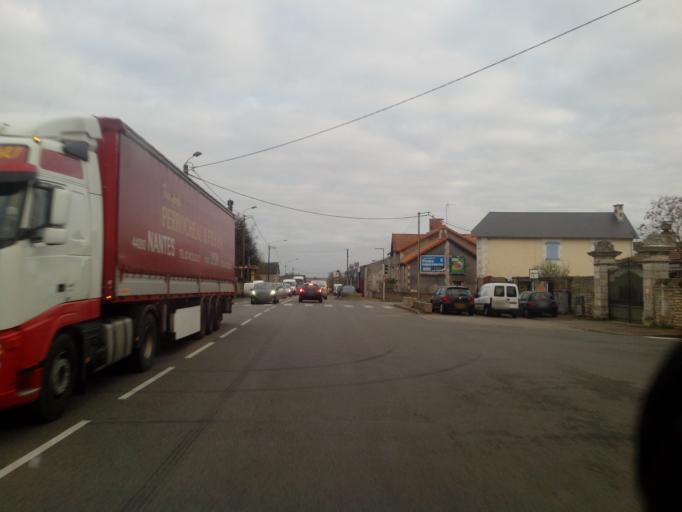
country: FR
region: Poitou-Charentes
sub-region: Departement de la Vienne
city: Vouille
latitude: 46.6466
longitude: 0.1699
